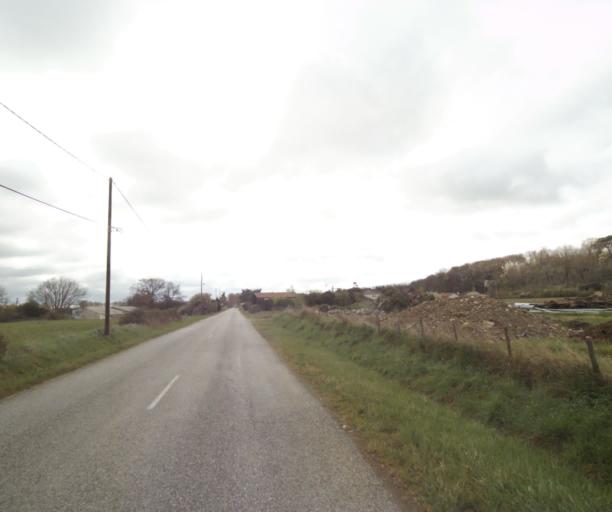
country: FR
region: Midi-Pyrenees
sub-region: Departement de l'Ariege
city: Saverdun
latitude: 43.2437
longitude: 1.5640
